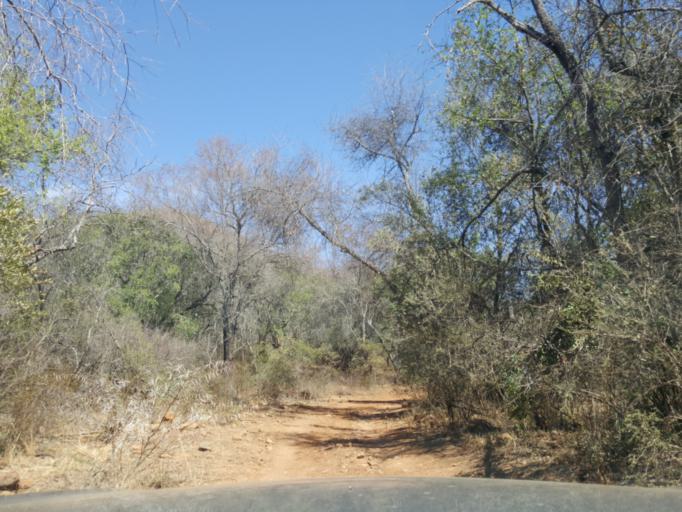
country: BW
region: South East
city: Lobatse
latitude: -25.1595
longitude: 25.6774
